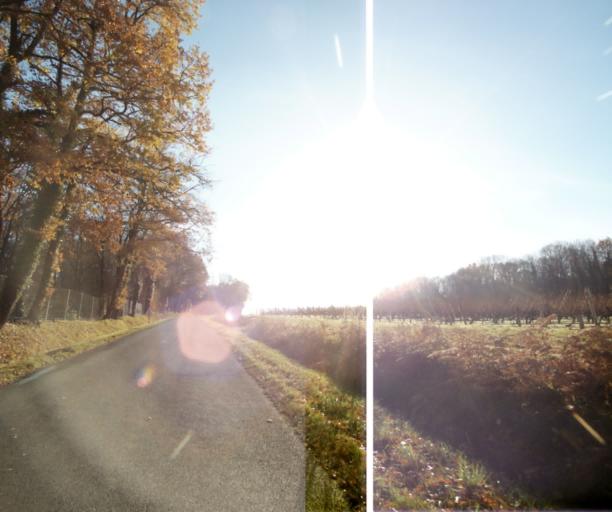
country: FR
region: Poitou-Charentes
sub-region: Departement de la Charente-Maritime
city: Cherac
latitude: 45.7379
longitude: -0.4366
